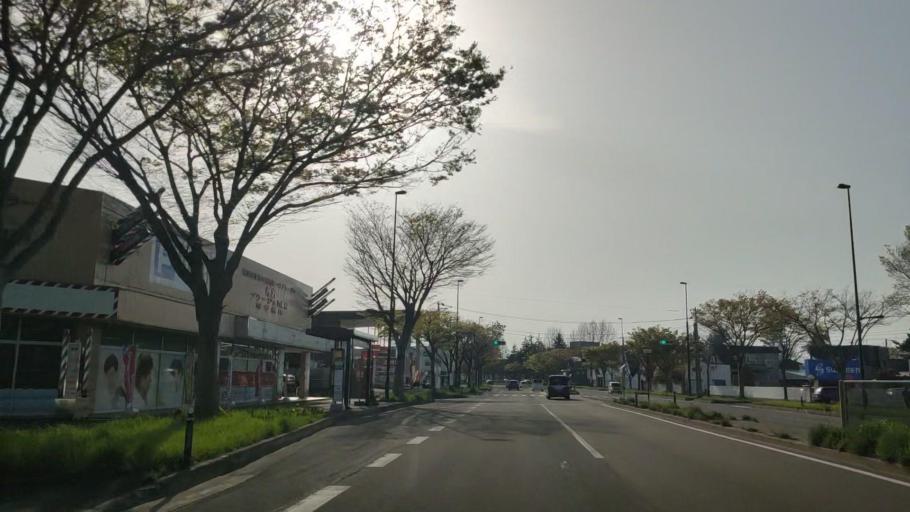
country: JP
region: Aomori
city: Aomori Shi
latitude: 40.8280
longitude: 140.7898
